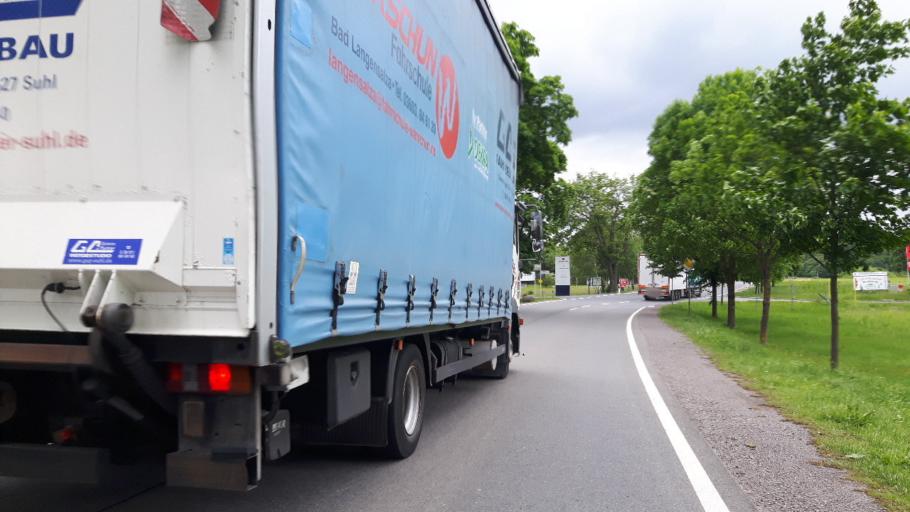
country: DE
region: Thuringia
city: Grossbreitenbach
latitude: 50.5845
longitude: 10.9951
